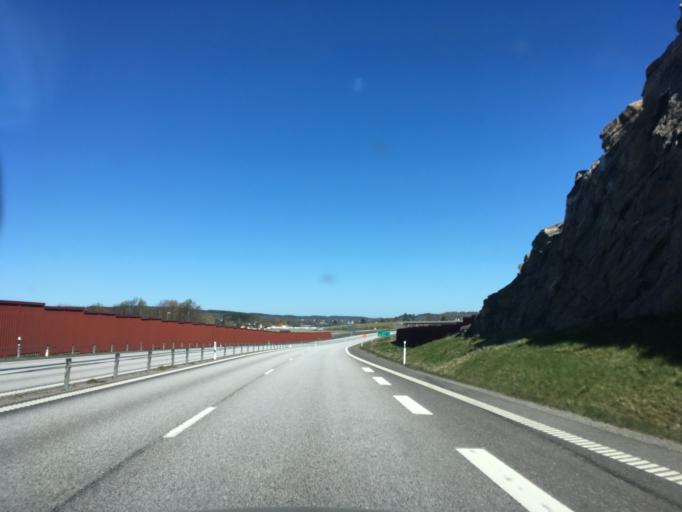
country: SE
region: Vaestra Goetaland
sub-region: Ale Kommun
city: Skepplanda
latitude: 57.9972
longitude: 12.1603
